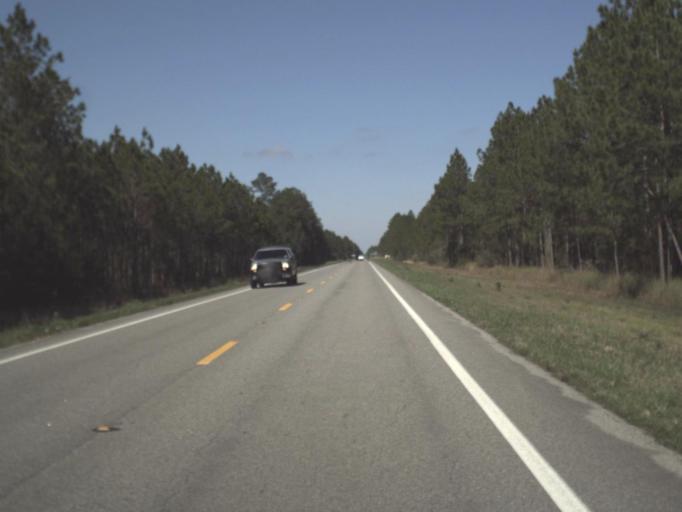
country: US
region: Florida
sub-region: Gulf County
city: Port Saint Joe
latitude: 29.9043
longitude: -85.2086
